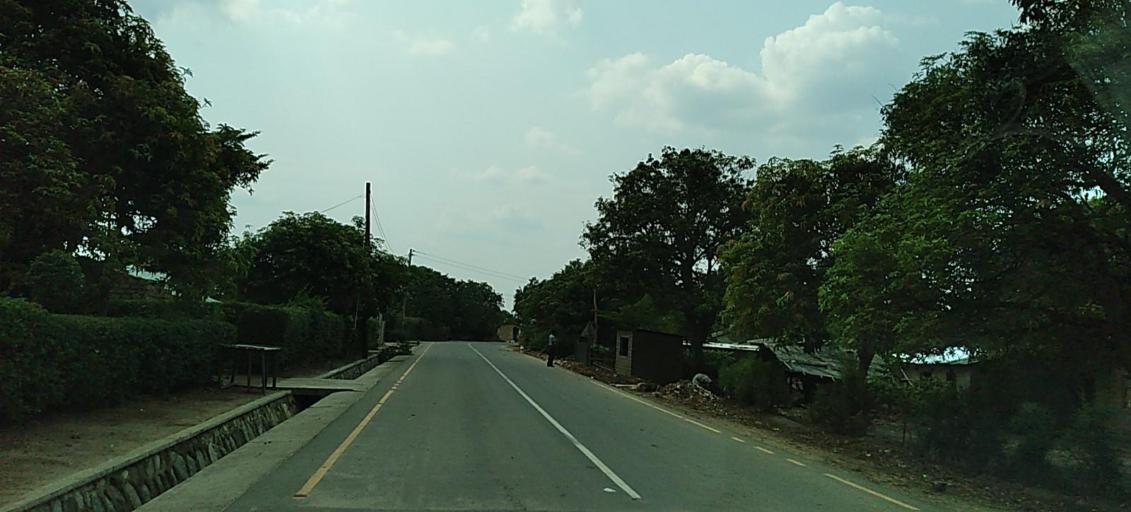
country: ZM
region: Copperbelt
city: Kalulushi
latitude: -12.8541
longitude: 28.1297
